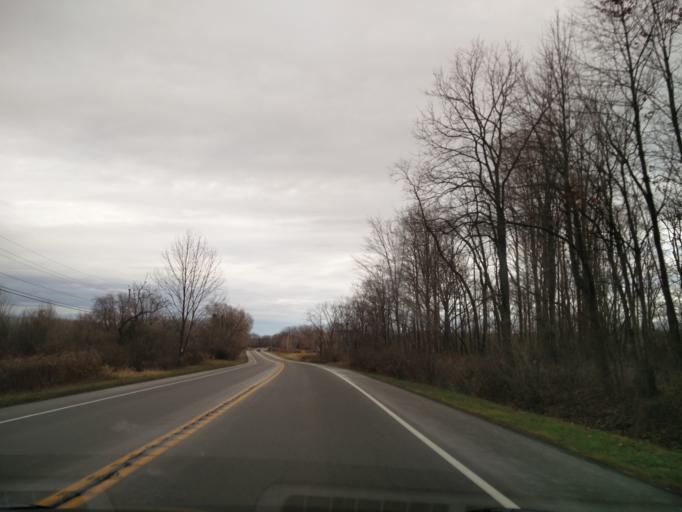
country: US
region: New York
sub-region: Tompkins County
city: Northwest Ithaca
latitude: 42.4985
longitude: -76.6014
